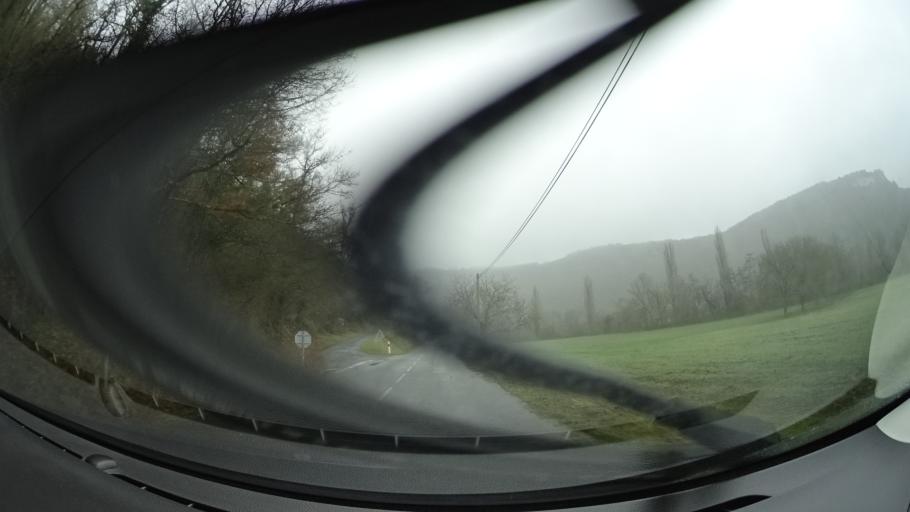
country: FR
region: Aquitaine
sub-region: Departement de la Dordogne
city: Cenac-et-Saint-Julien
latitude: 44.7971
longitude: 1.1602
